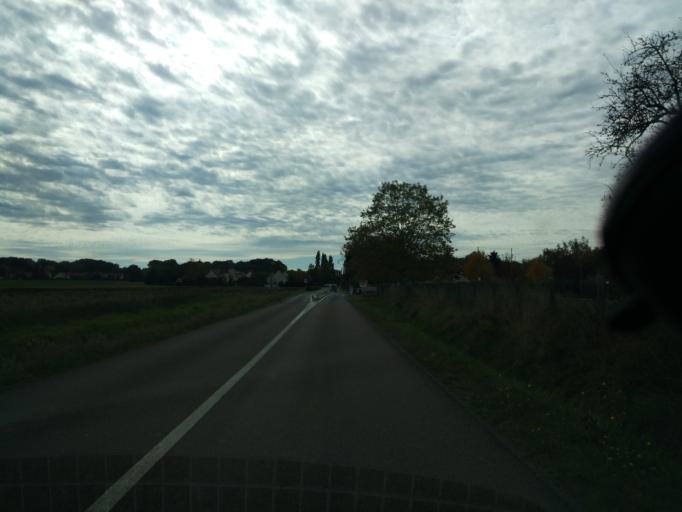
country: FR
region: Ile-de-France
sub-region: Departement de l'Essonne
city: Les Molieres
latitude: 48.6790
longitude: 2.0737
